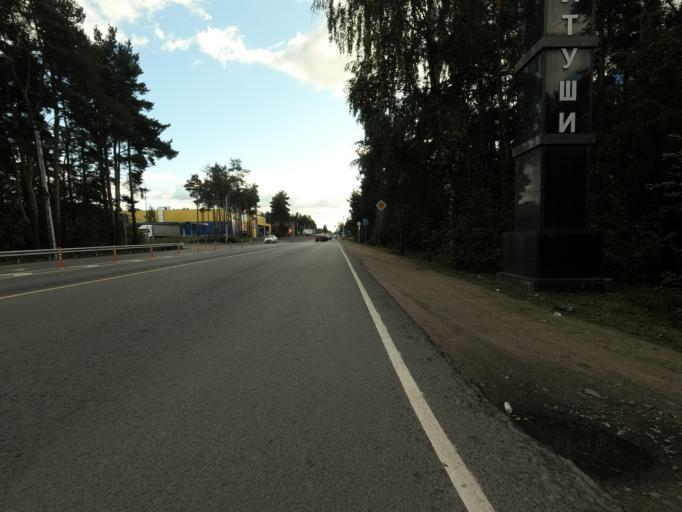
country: RU
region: Leningrad
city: Vsevolozhsk
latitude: 59.9926
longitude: 30.6585
